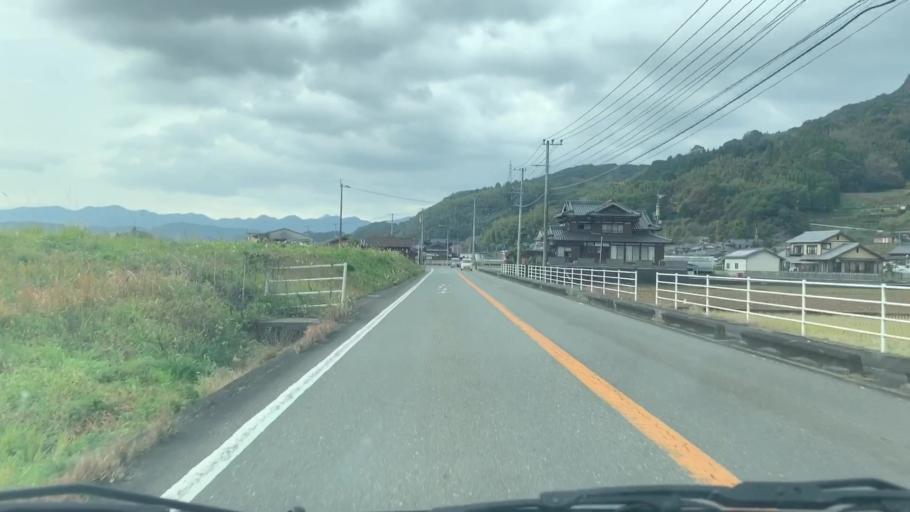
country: JP
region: Saga Prefecture
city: Ureshinomachi-shimojuku
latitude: 33.1360
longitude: 130.0169
